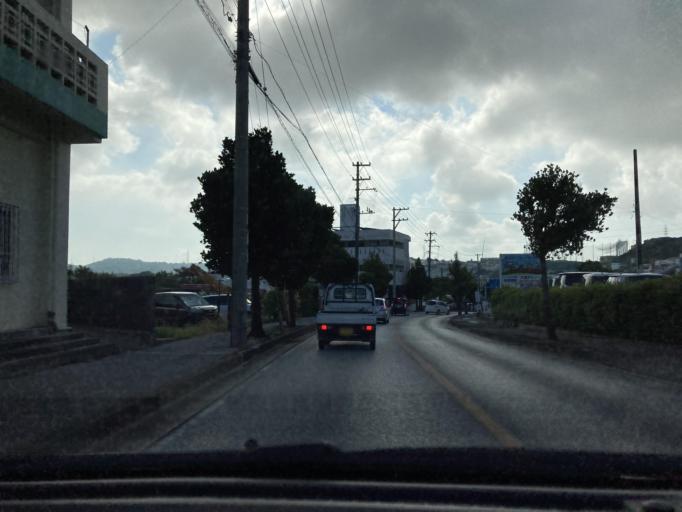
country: JP
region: Okinawa
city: Tomigusuku
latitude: 26.1717
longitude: 127.7364
